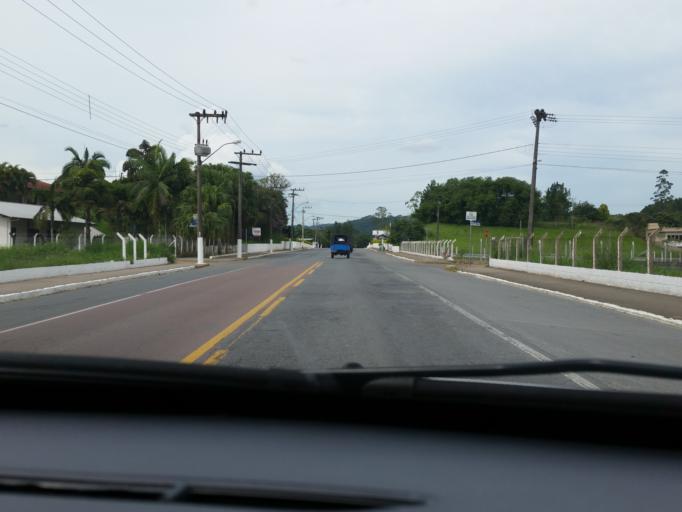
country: BR
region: Santa Catarina
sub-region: Rodeio
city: Gavea
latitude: -27.0306
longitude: -49.3832
